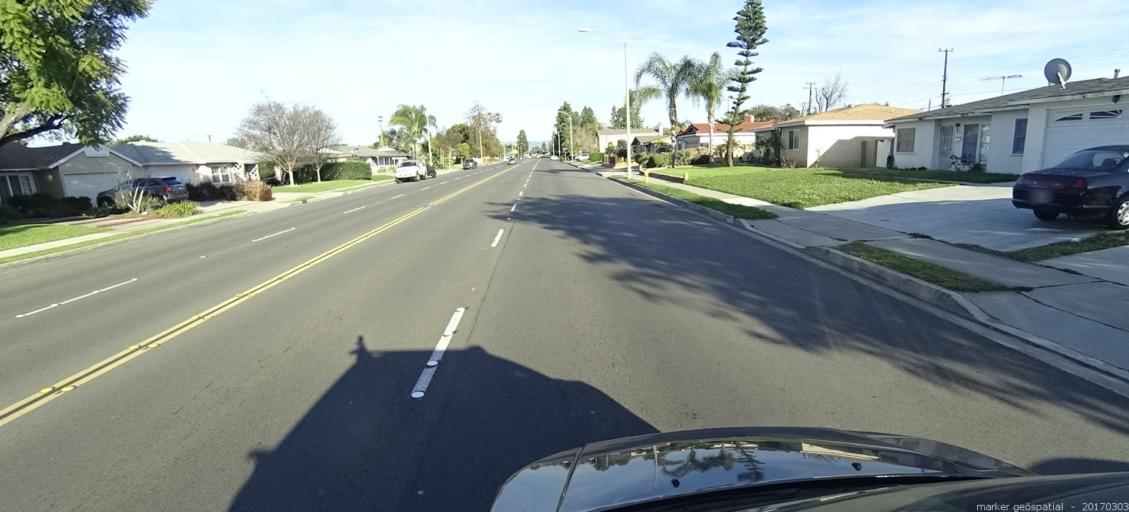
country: US
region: California
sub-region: Orange County
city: Anaheim
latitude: 33.8288
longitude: -117.9478
